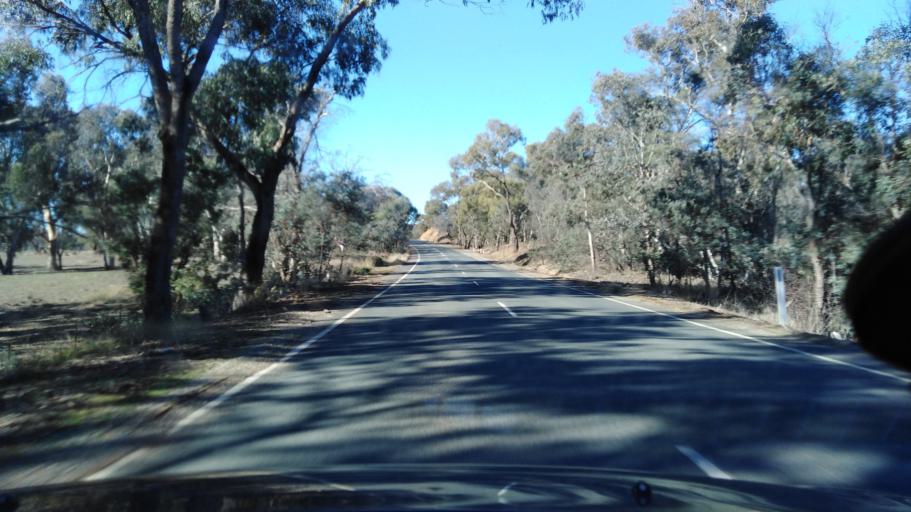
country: AU
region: New South Wales
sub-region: Yass Valley
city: Gundaroo
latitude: -35.1816
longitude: 149.2845
